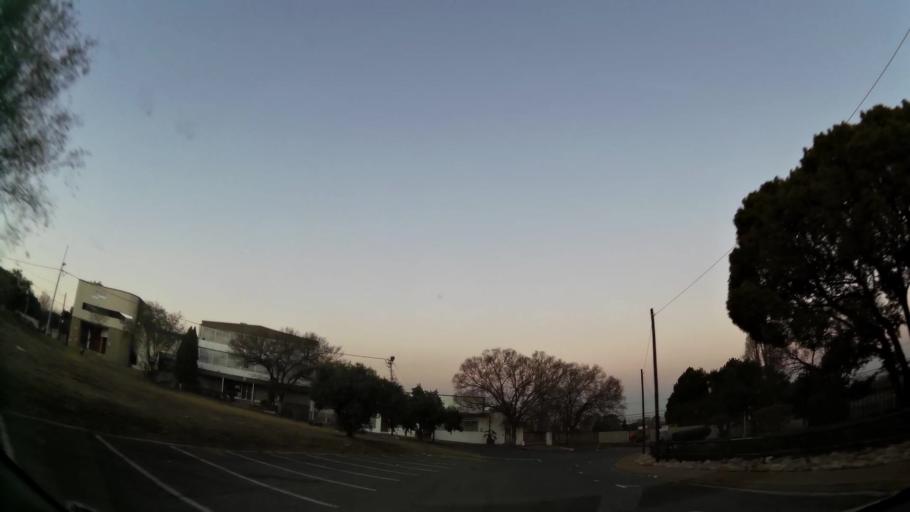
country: ZA
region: Gauteng
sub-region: City of Johannesburg Metropolitan Municipality
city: Roodepoort
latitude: -26.1779
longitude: 27.9302
